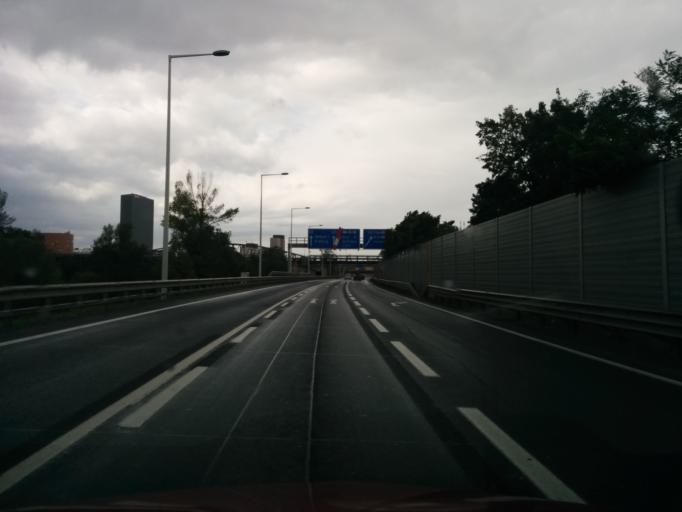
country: AT
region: Vienna
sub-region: Wien Stadt
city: Vienna
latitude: 48.1901
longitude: 16.4224
